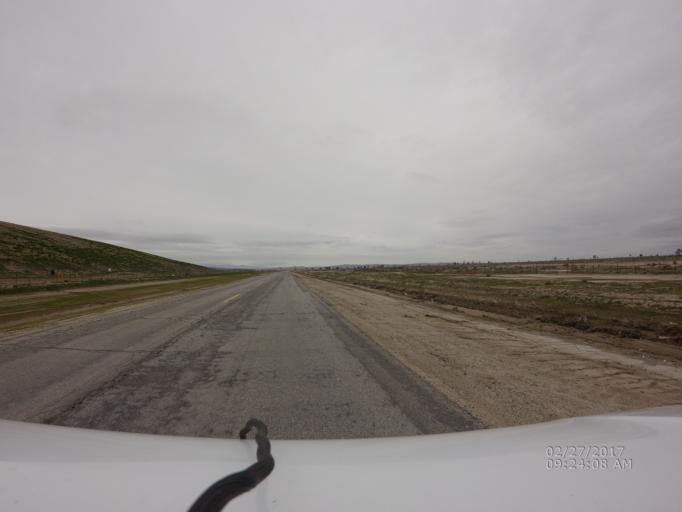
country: US
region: California
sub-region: Los Angeles County
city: Lancaster
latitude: 34.7463
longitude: -118.1131
